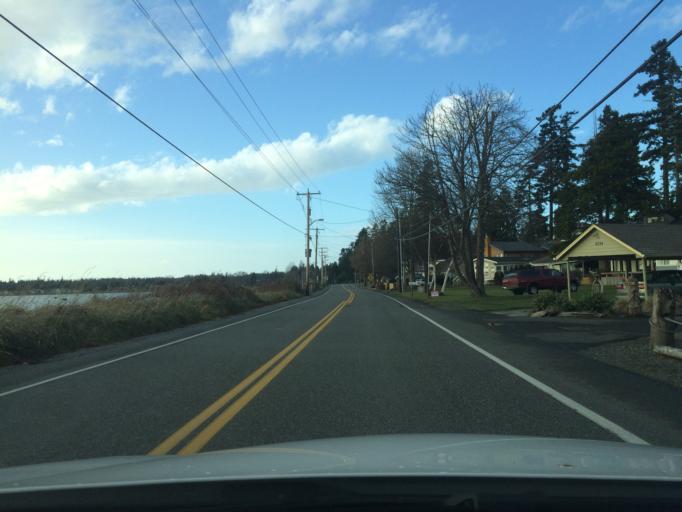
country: US
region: Washington
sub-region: Whatcom County
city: Birch Bay
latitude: 48.9412
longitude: -122.7619
